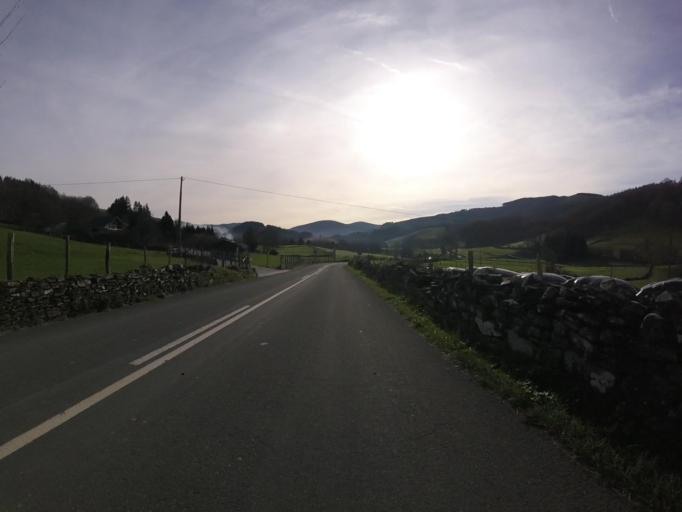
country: ES
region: Basque Country
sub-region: Provincia de Guipuzcoa
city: Berastegui
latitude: 43.1142
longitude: -1.9655
